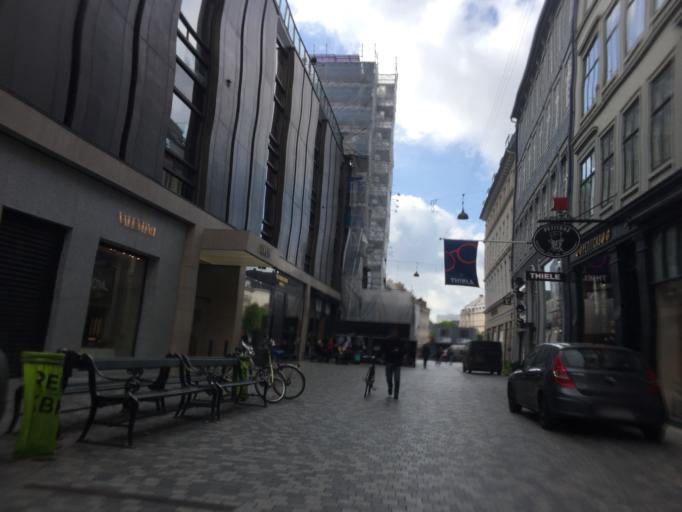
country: DK
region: Capital Region
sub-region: Kobenhavn
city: Copenhagen
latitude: 55.6795
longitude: 12.5793
